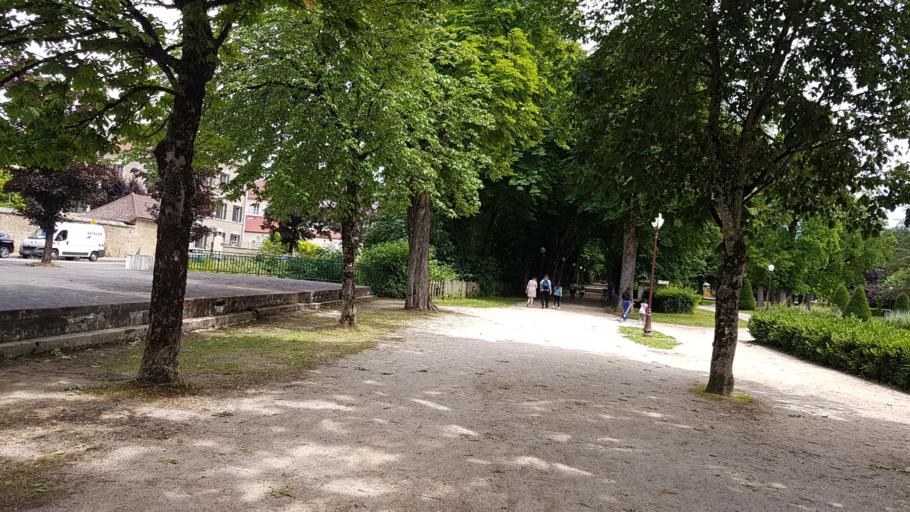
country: FR
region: Franche-Comte
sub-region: Departement du Jura
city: Lons-le-Saunier
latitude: 46.6730
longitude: 5.5599
